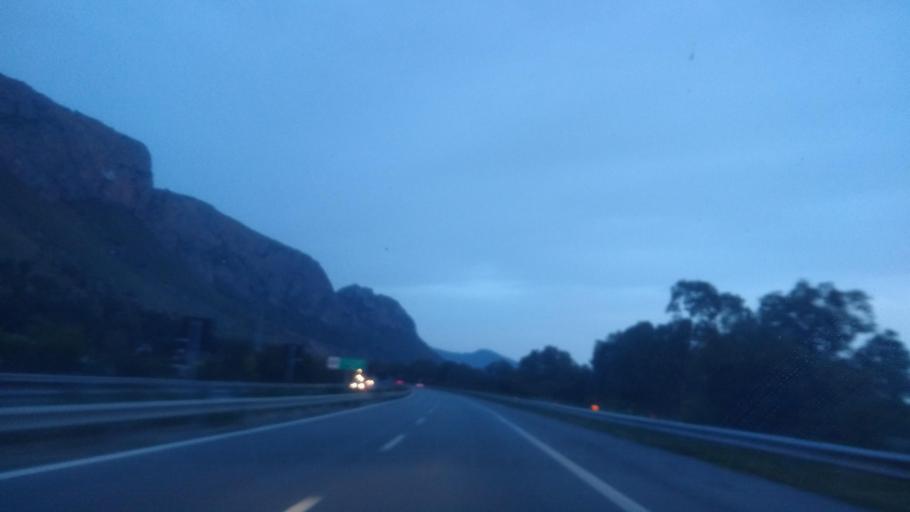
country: IT
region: Sicily
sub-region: Palermo
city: Agliandroni-Paternella
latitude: 38.1249
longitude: 13.0754
